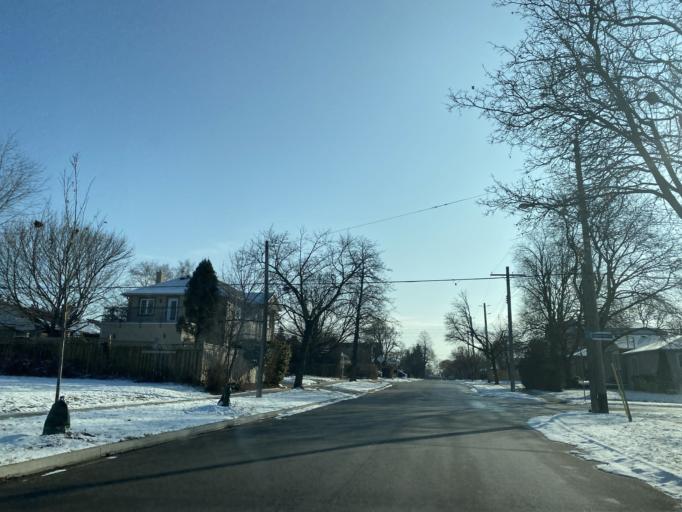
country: CA
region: Ontario
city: Etobicoke
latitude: 43.6662
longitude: -79.5635
